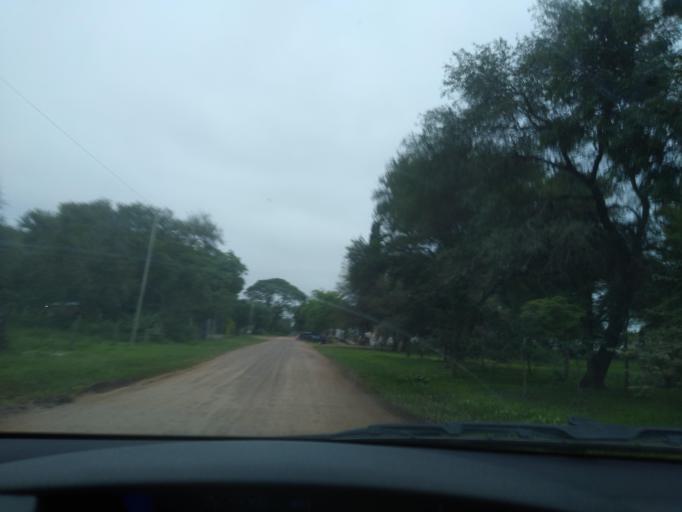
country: AR
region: Chaco
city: Colonia Benitez
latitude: -27.3308
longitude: -58.9630
